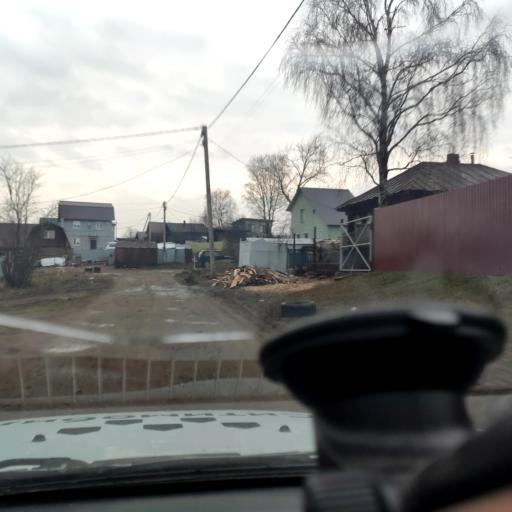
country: RU
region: Perm
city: Froly
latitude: 57.9305
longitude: 56.2332
